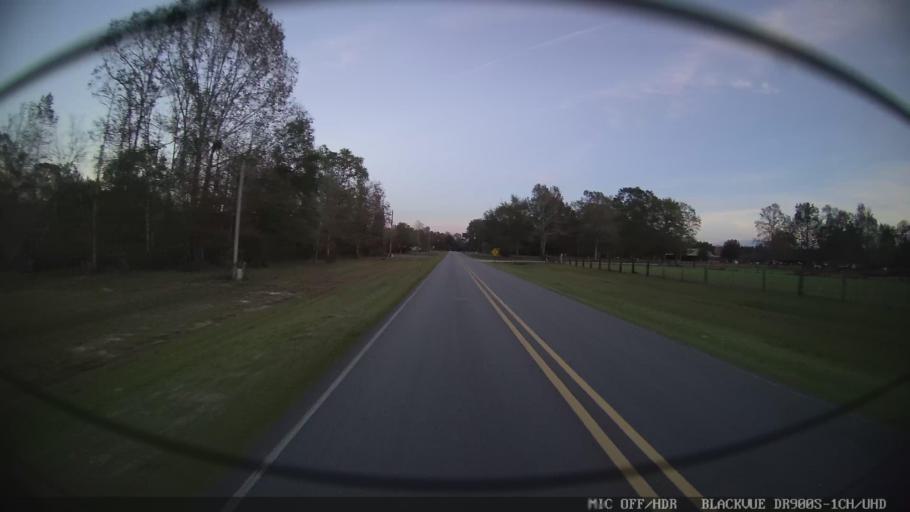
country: US
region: Mississippi
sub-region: Perry County
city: New Augusta
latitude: 31.0706
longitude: -89.1985
